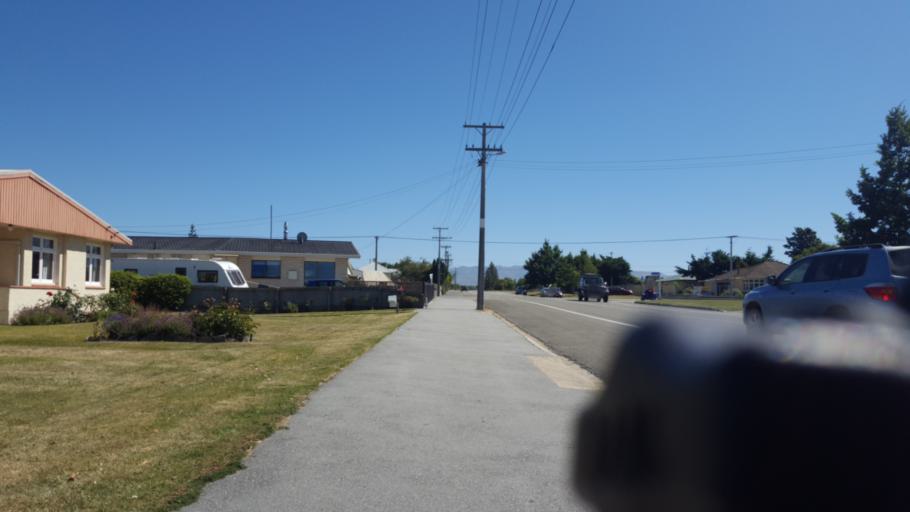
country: NZ
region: Otago
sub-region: Dunedin City
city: Dunedin
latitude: -45.1275
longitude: 170.1005
